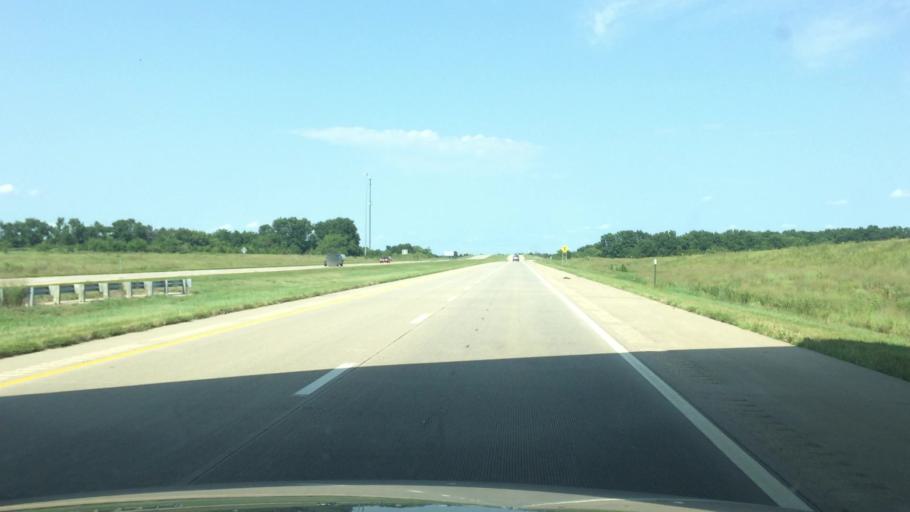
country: US
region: Kansas
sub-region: Linn County
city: Pleasanton
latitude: 38.1462
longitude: -94.7065
